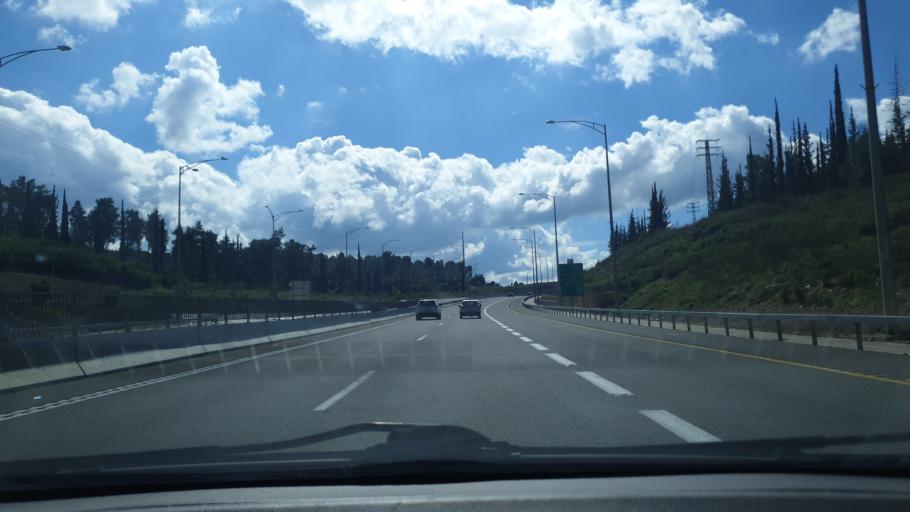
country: IL
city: Mevo horon
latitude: 31.7981
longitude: 35.0146
